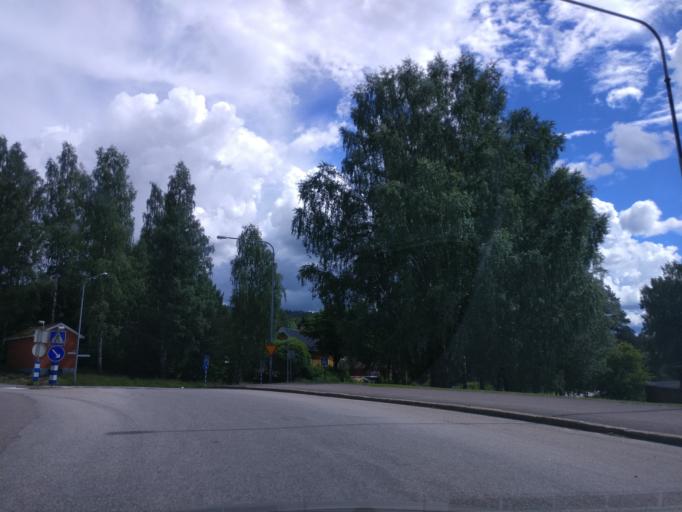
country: SE
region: Vaermland
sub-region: Hagfors Kommun
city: Hagfors
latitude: 60.0281
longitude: 13.6984
